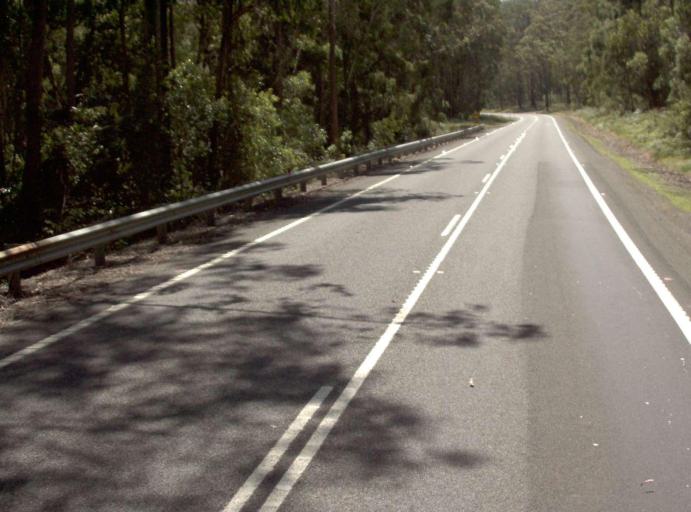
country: AU
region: New South Wales
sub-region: Bombala
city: Bombala
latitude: -37.5647
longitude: 149.0725
